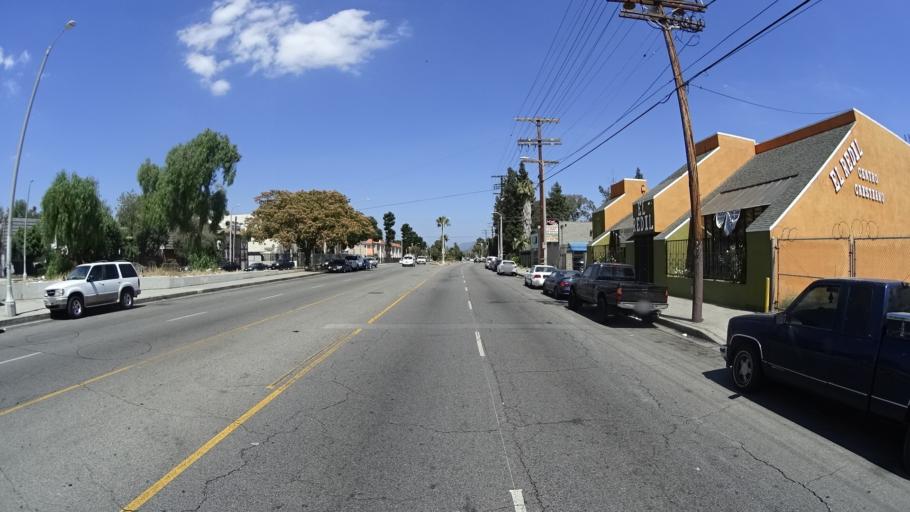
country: US
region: California
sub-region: Los Angeles County
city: Van Nuys
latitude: 34.2282
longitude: -118.4646
